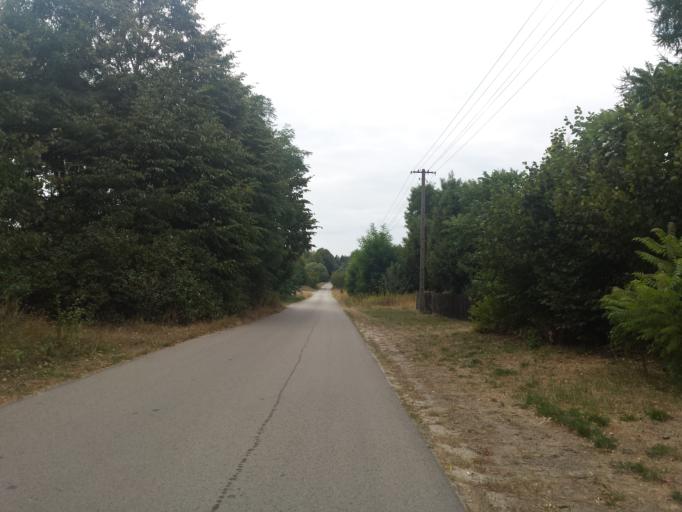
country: PL
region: Swietokrzyskie
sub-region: Powiat staszowski
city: Bogoria
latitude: 50.6589
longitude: 21.1915
